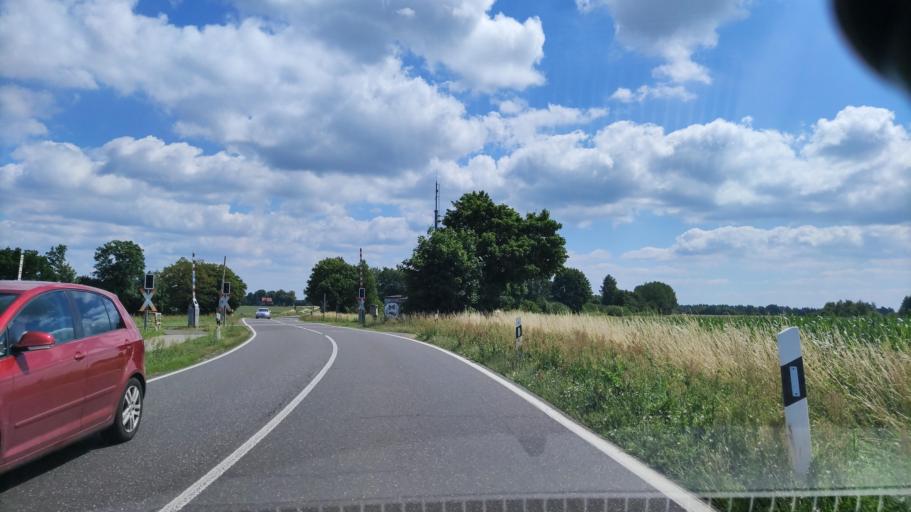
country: DE
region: Mecklenburg-Vorpommern
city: Hagenow
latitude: 53.4497
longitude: 11.1713
